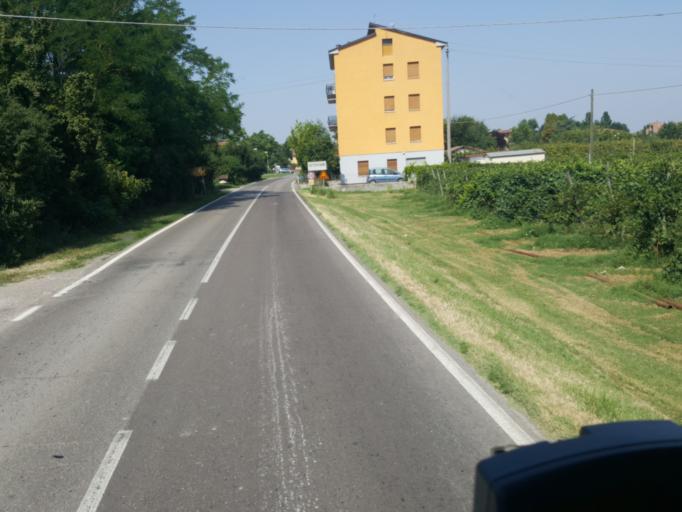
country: IT
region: Emilia-Romagna
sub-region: Provincia di Modena
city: Ca' di Sola
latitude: 44.5412
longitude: 10.9603
